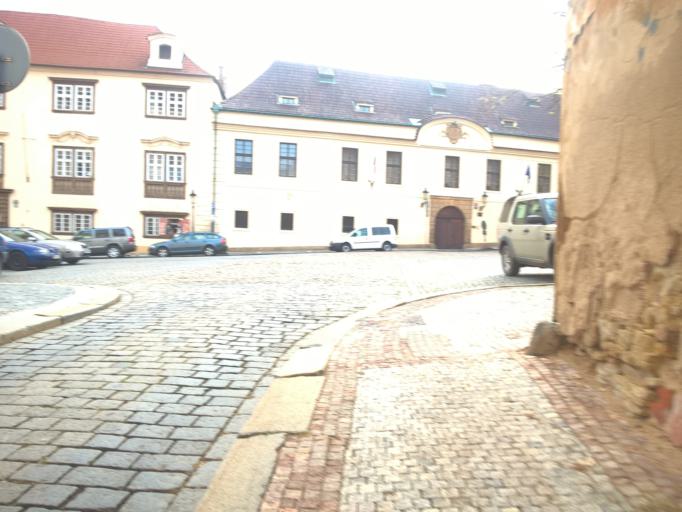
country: CZ
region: Praha
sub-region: Praha 1
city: Mala Strana
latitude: 50.0890
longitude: 14.3941
